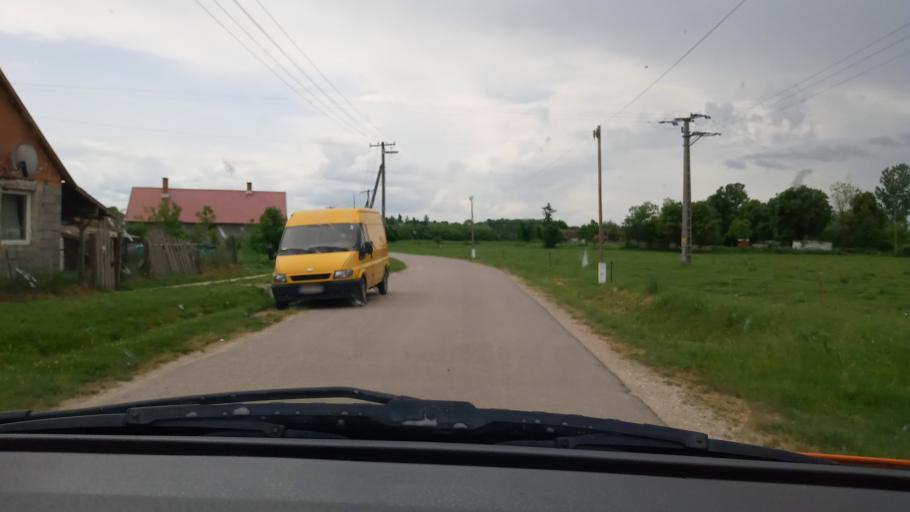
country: HU
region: Baranya
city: Vajszlo
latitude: 45.8235
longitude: 17.9935
